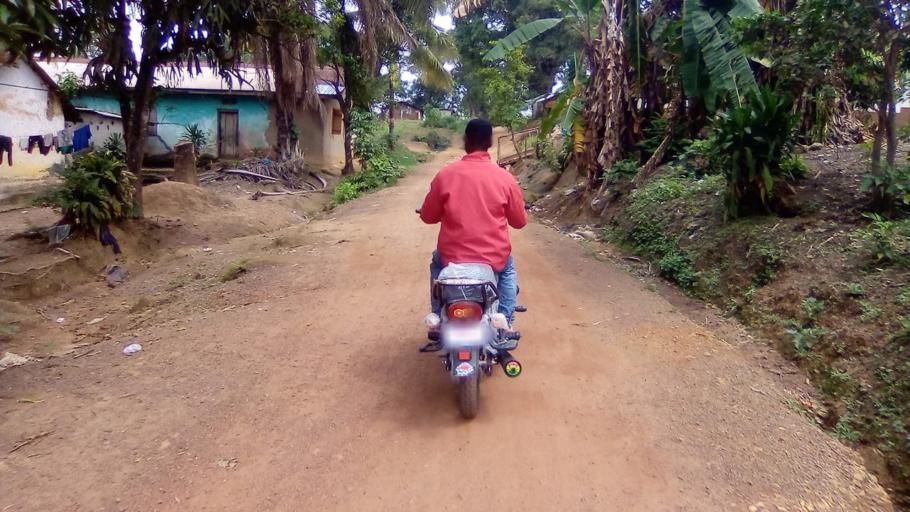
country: SL
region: Southern Province
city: Bo
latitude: 7.9625
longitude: -11.7236
